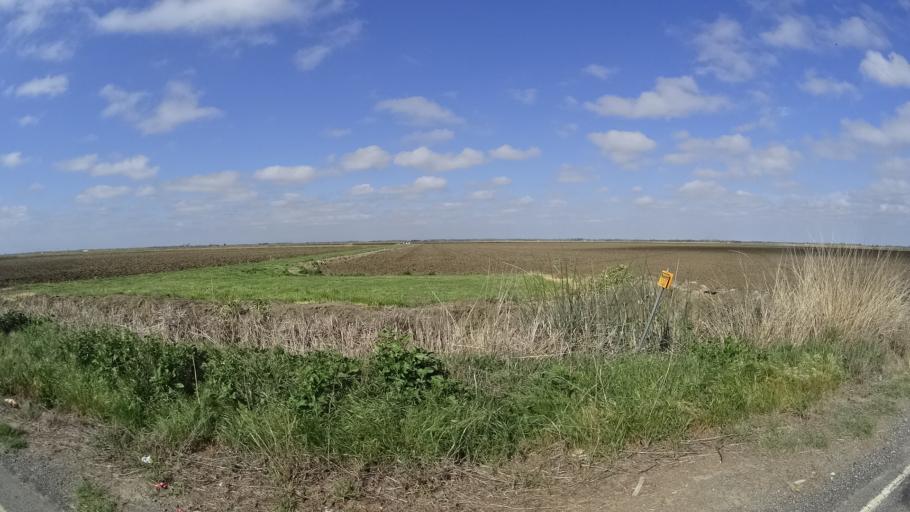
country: US
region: California
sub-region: Colusa County
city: Colusa
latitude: 39.3699
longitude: -121.9363
